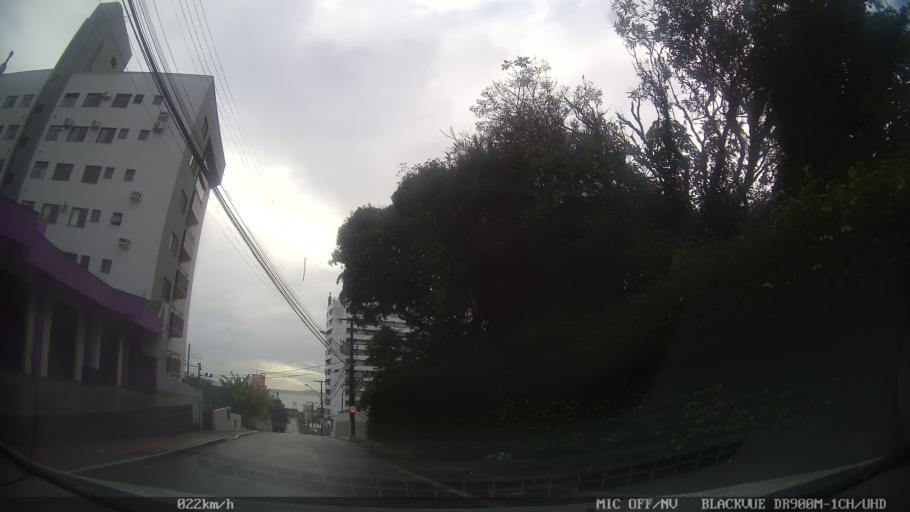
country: BR
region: Santa Catarina
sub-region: Sao Jose
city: Campinas
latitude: -27.5753
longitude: -48.6048
